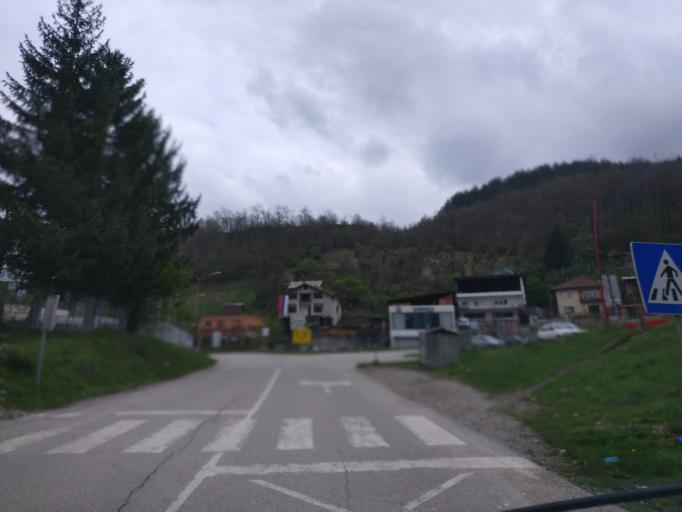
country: BA
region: Republika Srpska
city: Foca
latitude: 43.4864
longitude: 18.7461
